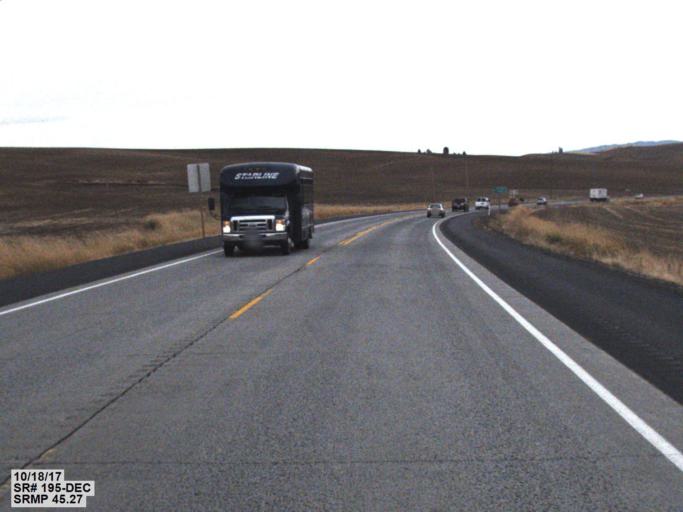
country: US
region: Washington
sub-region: Whitman County
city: Colfax
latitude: 46.9750
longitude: -117.3267
